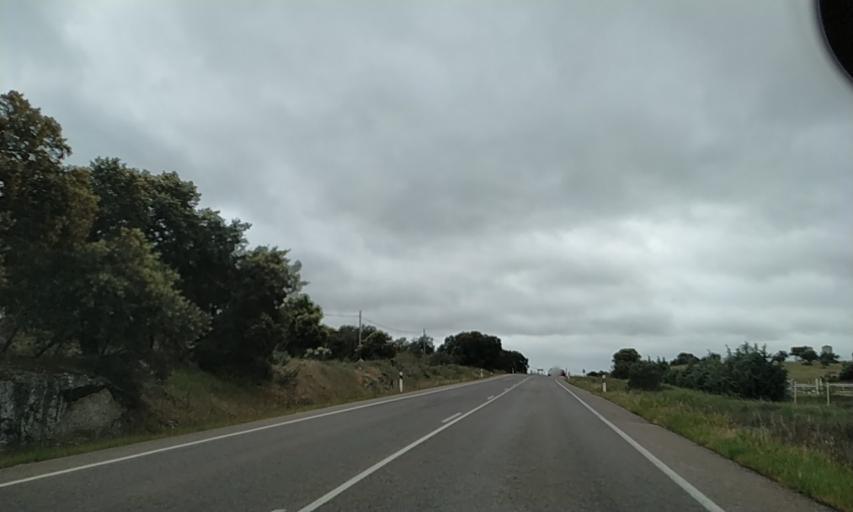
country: ES
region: Extremadura
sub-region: Provincia de Caceres
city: Caceres
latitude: 39.4129
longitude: -6.4145
